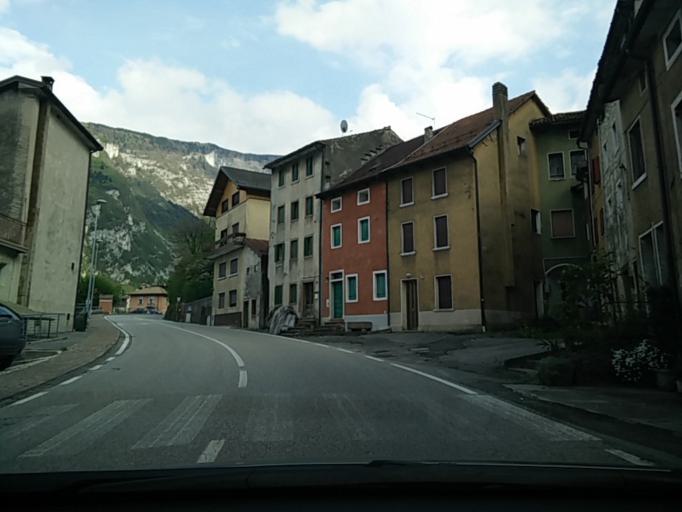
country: IT
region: Veneto
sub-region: Provincia di Belluno
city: Farra d'Alpago
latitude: 46.0921
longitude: 12.3302
